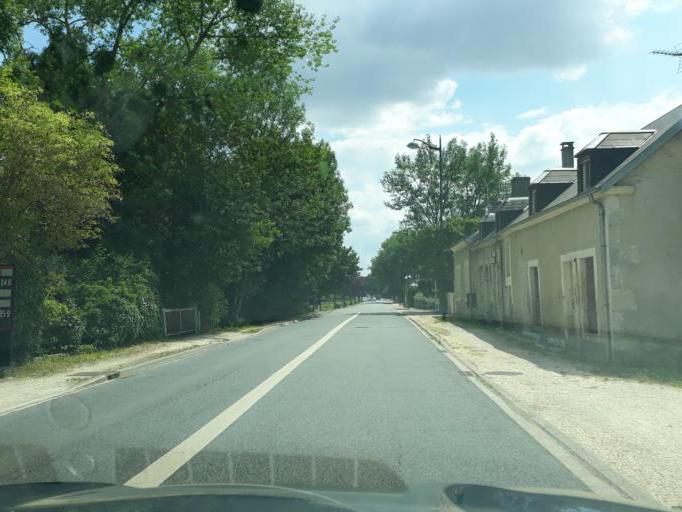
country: FR
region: Centre
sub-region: Departement du Cher
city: Avord
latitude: 47.0439
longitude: 2.5638
